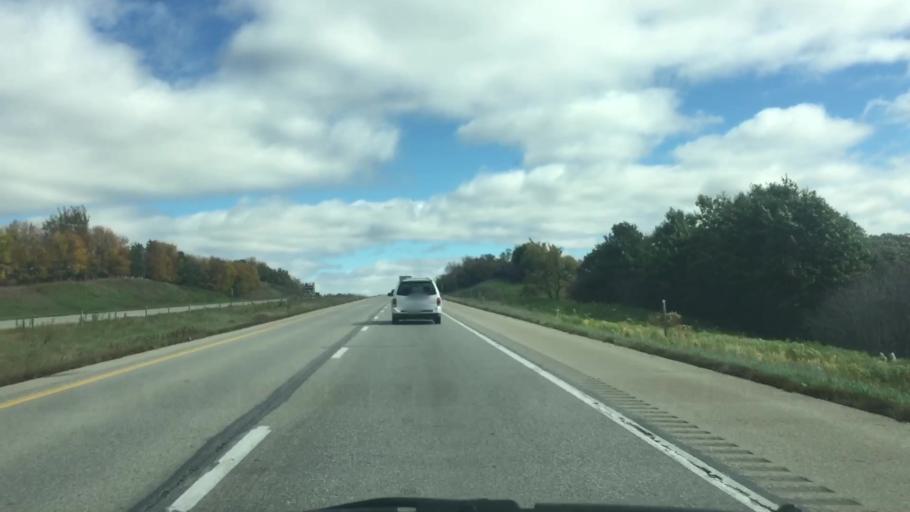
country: US
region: Iowa
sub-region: Poweshiek County
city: Grinnell
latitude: 41.6951
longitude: -92.8383
